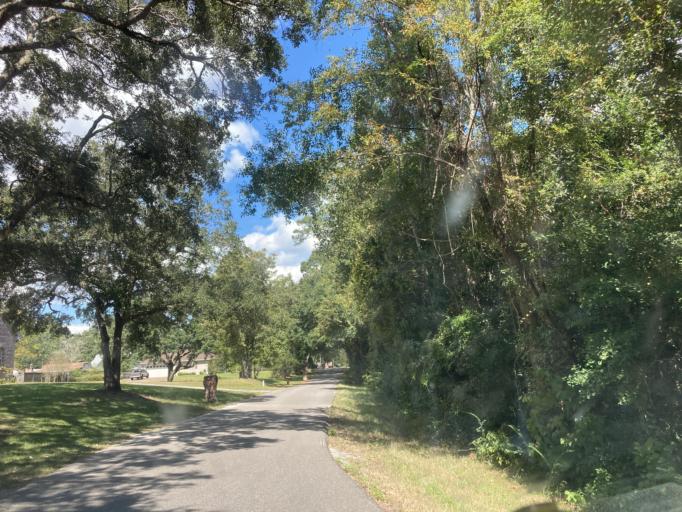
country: US
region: Mississippi
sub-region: Jackson County
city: Gulf Hills
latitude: 30.4444
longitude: -88.8424
